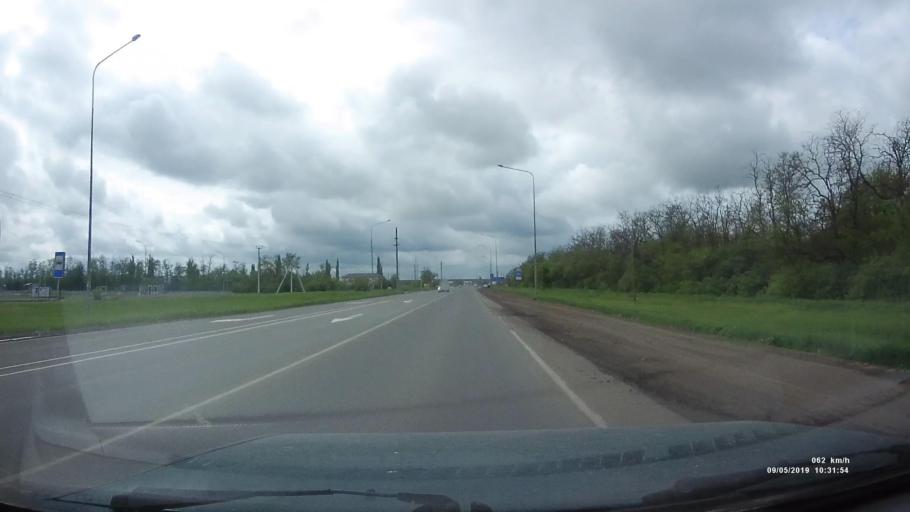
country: RU
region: Rostov
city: Azov
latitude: 47.0775
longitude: 39.4272
